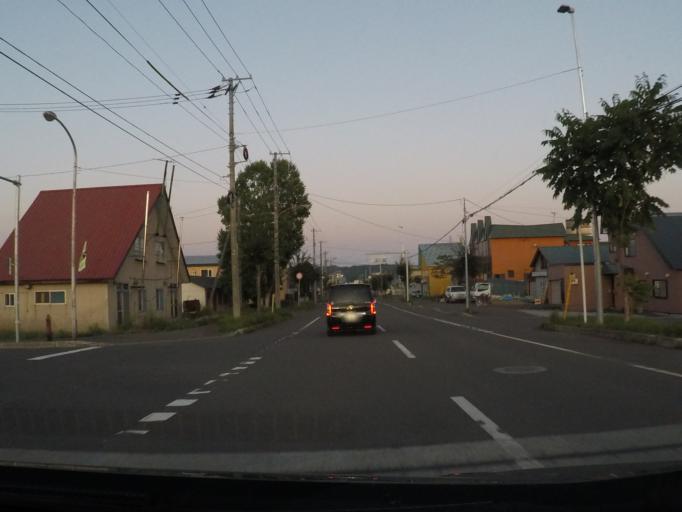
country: JP
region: Hokkaido
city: Nayoro
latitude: 44.3464
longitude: 142.4456
